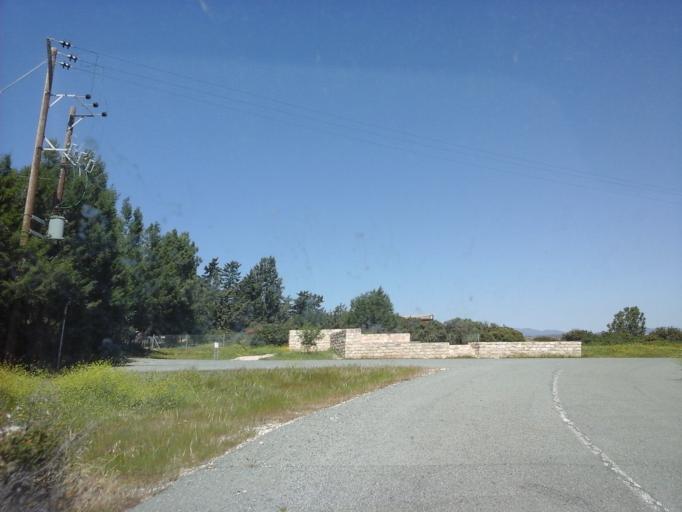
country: CY
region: Limassol
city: Sotira
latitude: 34.6717
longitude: 32.8639
